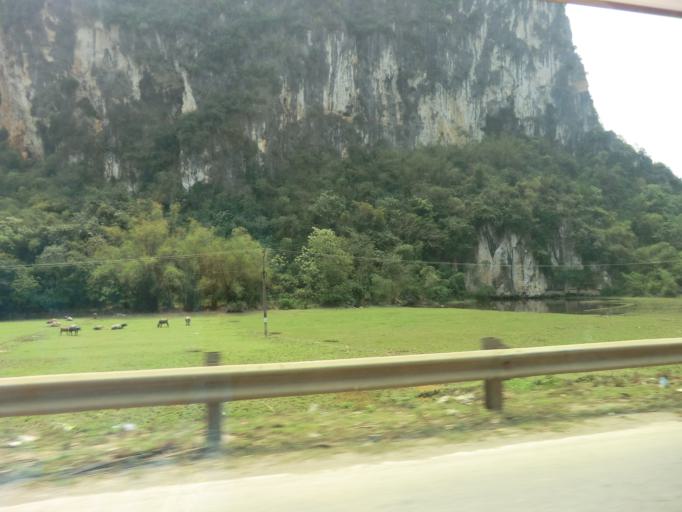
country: VN
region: Thanh Hoa
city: Thi Tran Cam Thuy
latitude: 20.2173
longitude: 105.4883
